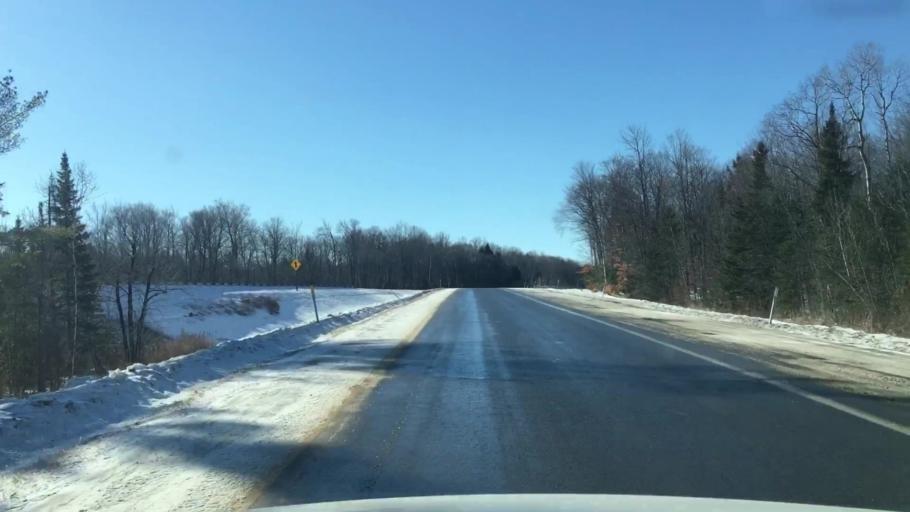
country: US
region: Maine
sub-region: Kennebec County
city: Clinton
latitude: 44.6395
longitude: -69.5300
